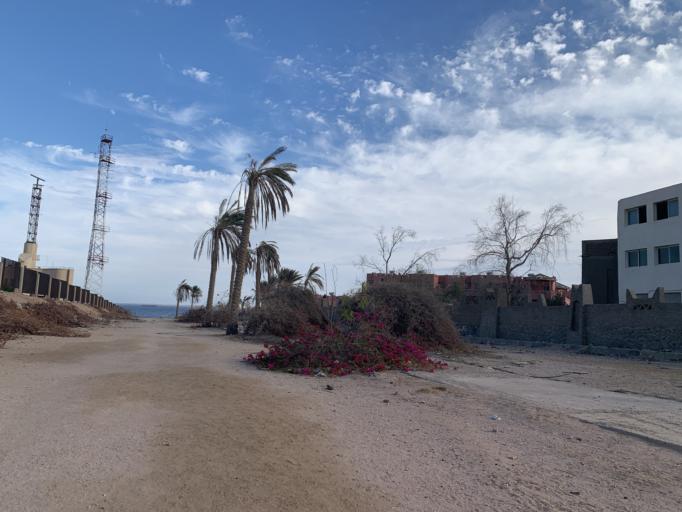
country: EG
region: South Sinai
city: Sharm el-Sheikh
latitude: 28.0175
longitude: 34.4355
